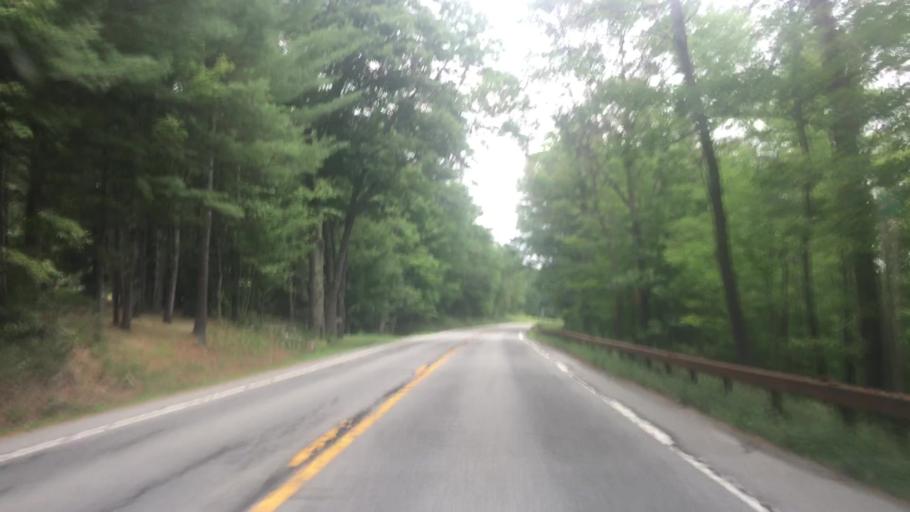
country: US
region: New York
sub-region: Essex County
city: Elizabethtown
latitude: 44.3950
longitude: -73.7093
